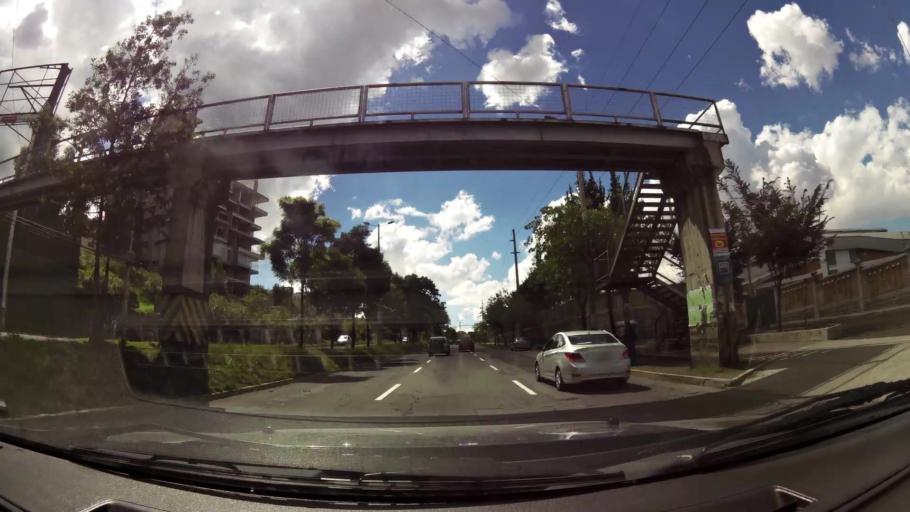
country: EC
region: Pichincha
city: Quito
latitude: -0.1541
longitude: -78.4974
